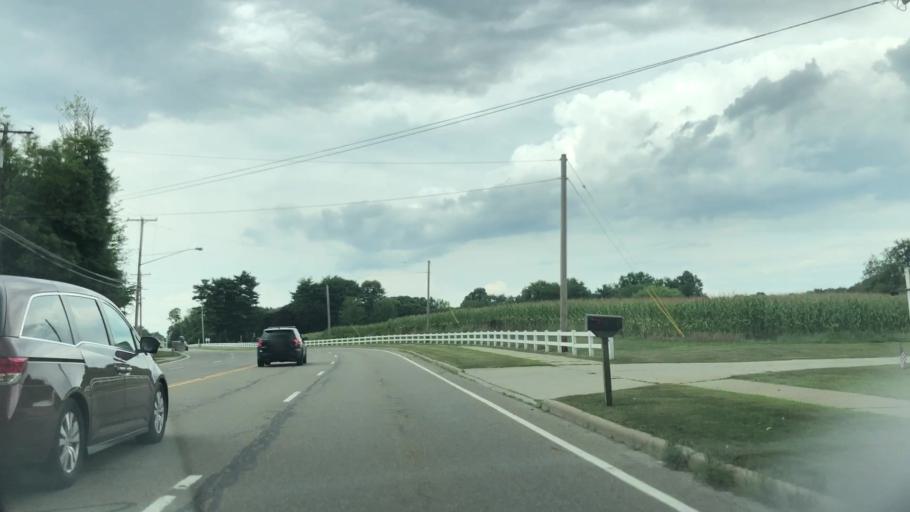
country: US
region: Ohio
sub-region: Summit County
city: Portage Lakes
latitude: 40.9903
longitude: -81.5216
